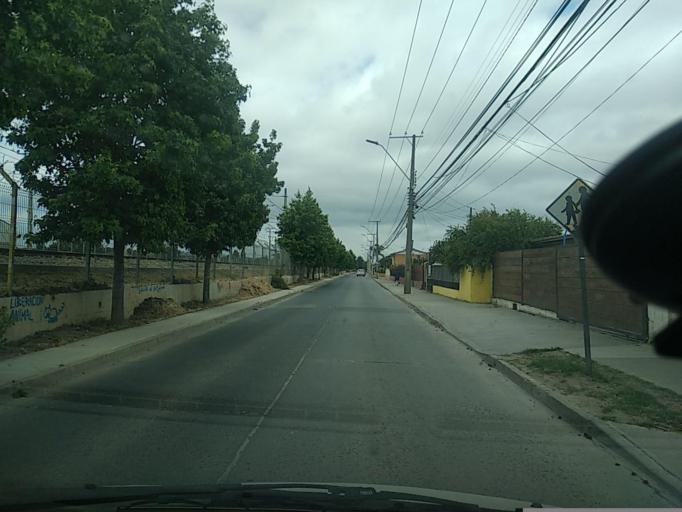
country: CL
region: Valparaiso
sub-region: Provincia de Marga Marga
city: Villa Alemana
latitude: -33.0415
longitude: -71.3609
